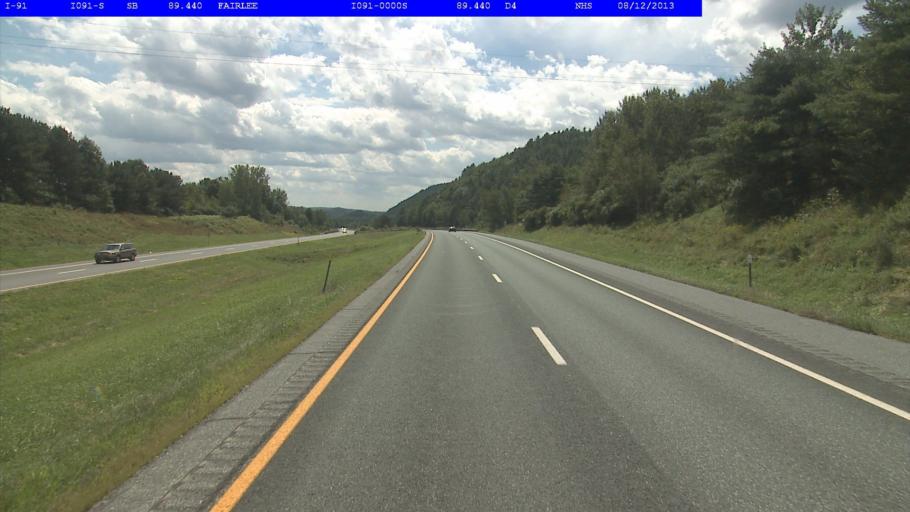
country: US
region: New Hampshire
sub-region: Grafton County
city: Orford
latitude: 43.8830
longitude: -72.1785
